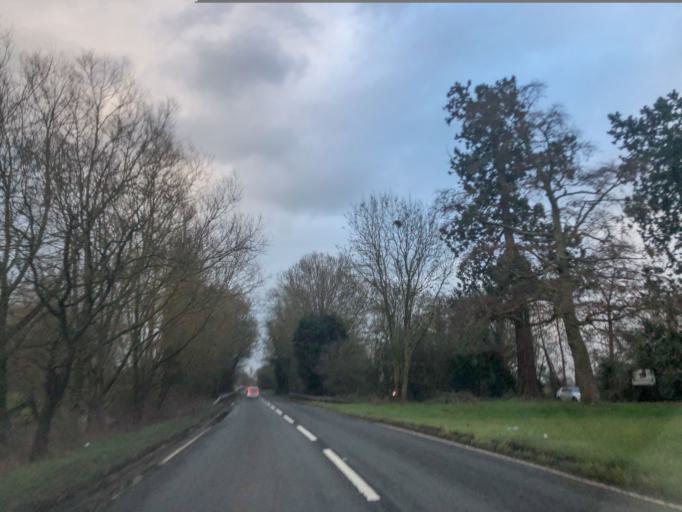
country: GB
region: England
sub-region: Solihull
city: Hampton in Arden
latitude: 52.4412
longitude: -1.6844
